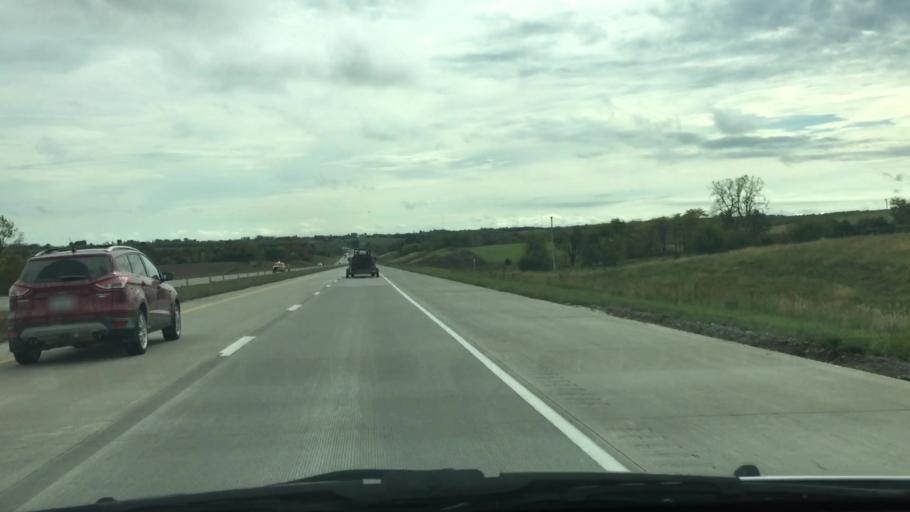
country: US
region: Iowa
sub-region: Warren County
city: Norwalk
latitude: 41.3402
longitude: -93.7778
